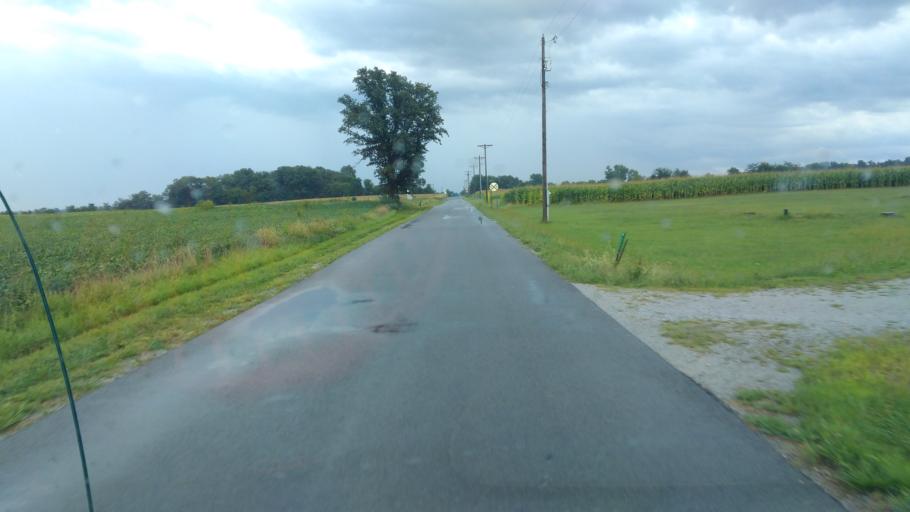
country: US
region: Ohio
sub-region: Hardin County
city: Kenton
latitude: 40.6896
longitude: -83.6469
